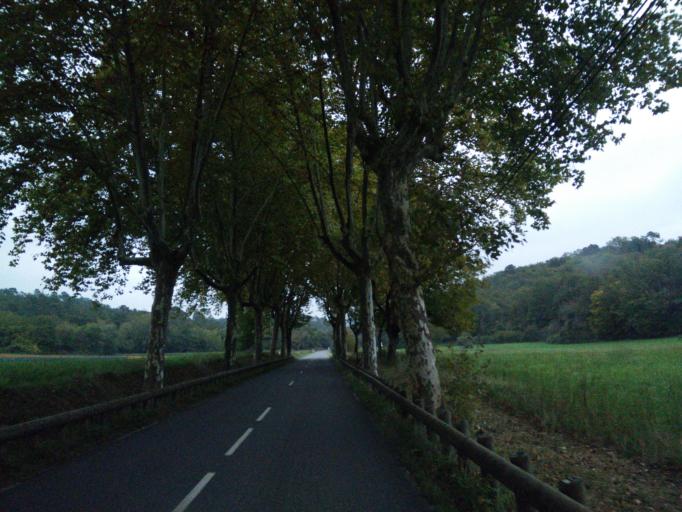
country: FR
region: Midi-Pyrenees
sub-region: Departement du Lot
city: Gourdon
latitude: 44.7756
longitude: 1.3324
